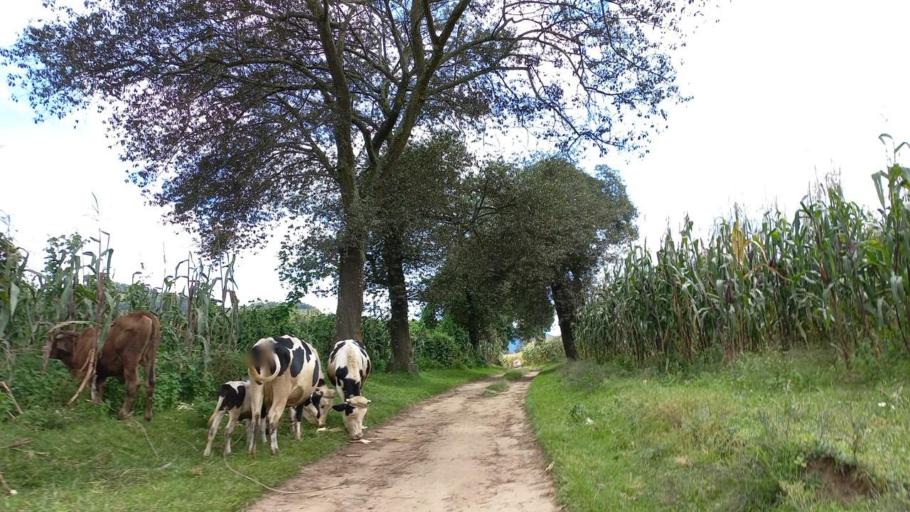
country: GT
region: Totonicapan
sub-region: Municipio de San Andres Xecul
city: San Andres Xecul
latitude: 14.8942
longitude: -91.4738
